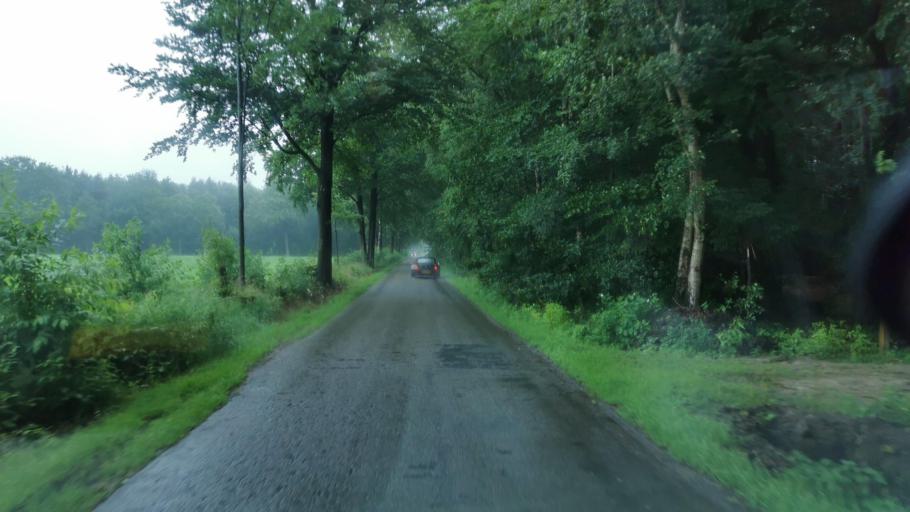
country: NL
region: Overijssel
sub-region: Gemeente Losser
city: Losser
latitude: 52.2429
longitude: 6.9512
